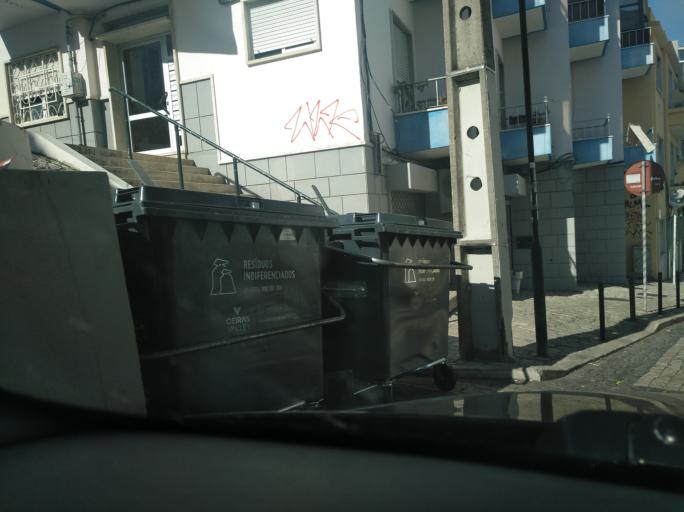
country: PT
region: Lisbon
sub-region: Oeiras
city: Alges
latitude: 38.7067
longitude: -9.2294
